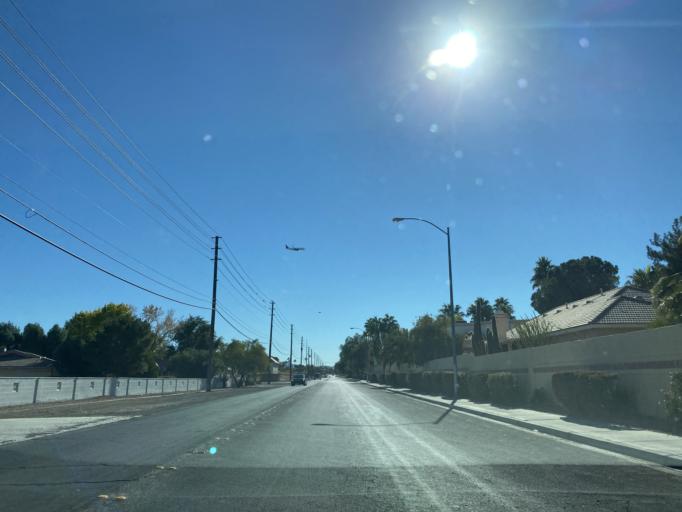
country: US
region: Nevada
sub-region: Clark County
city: Whitney
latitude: 36.0832
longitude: -115.0868
